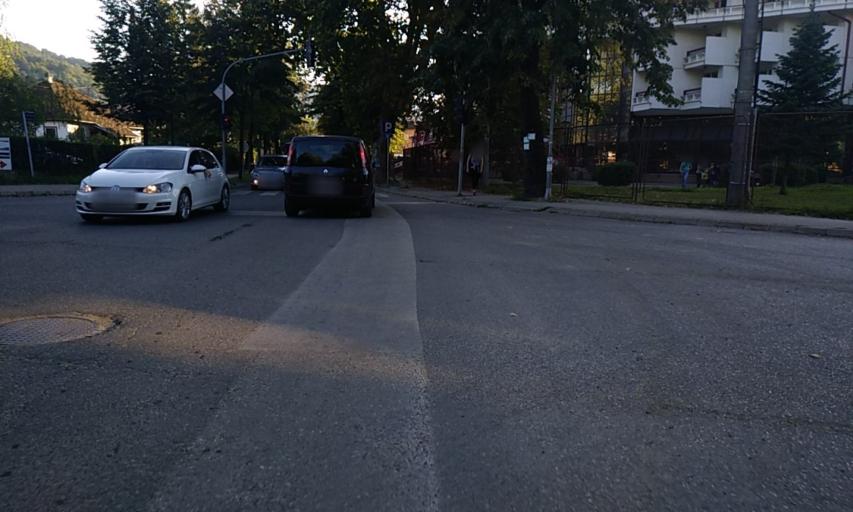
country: BA
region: Republika Srpska
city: Hiseti
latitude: 44.7599
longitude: 17.1848
